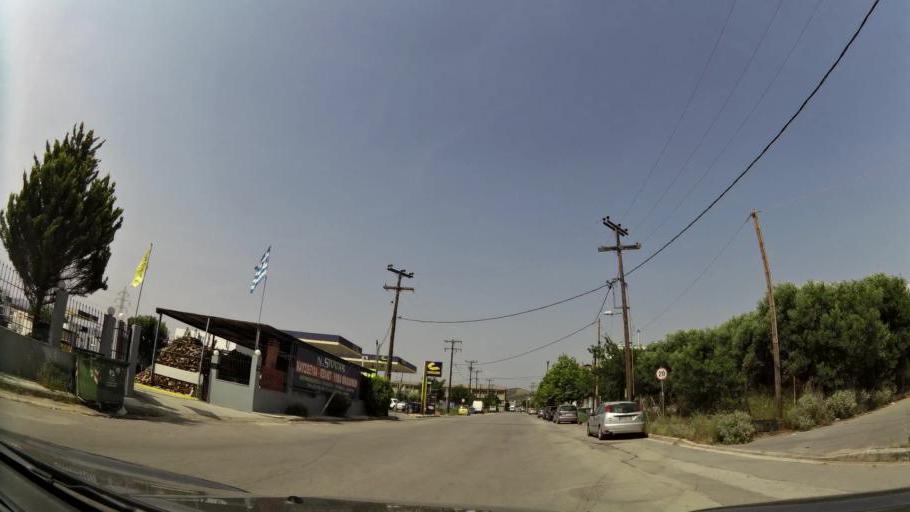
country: GR
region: Central Macedonia
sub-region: Nomos Thessalonikis
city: Efkarpia
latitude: 40.6885
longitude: 22.9484
